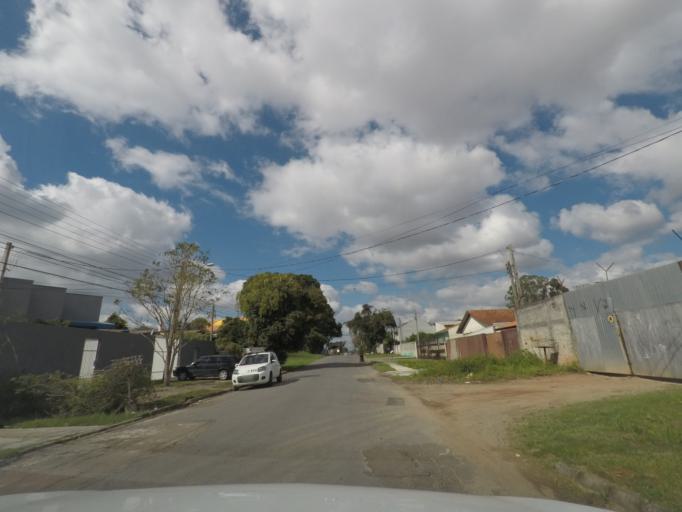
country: BR
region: Parana
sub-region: Sao Jose Dos Pinhais
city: Sao Jose dos Pinhais
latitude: -25.5004
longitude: -49.2284
